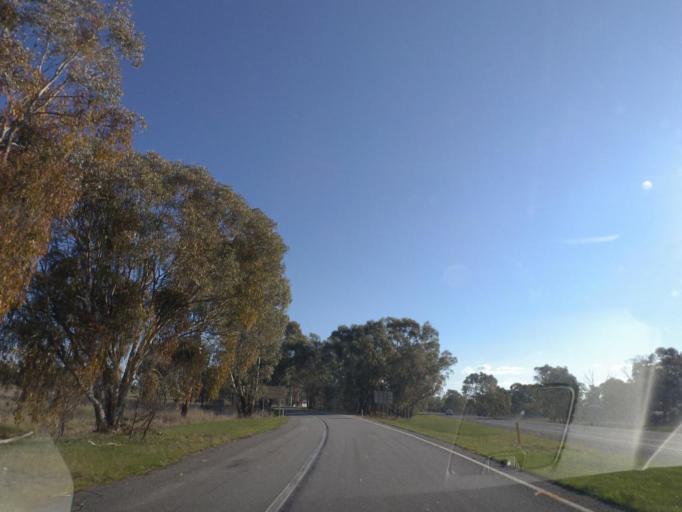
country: AU
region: Victoria
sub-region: Benalla
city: Benalla
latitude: -36.5767
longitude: 145.9232
